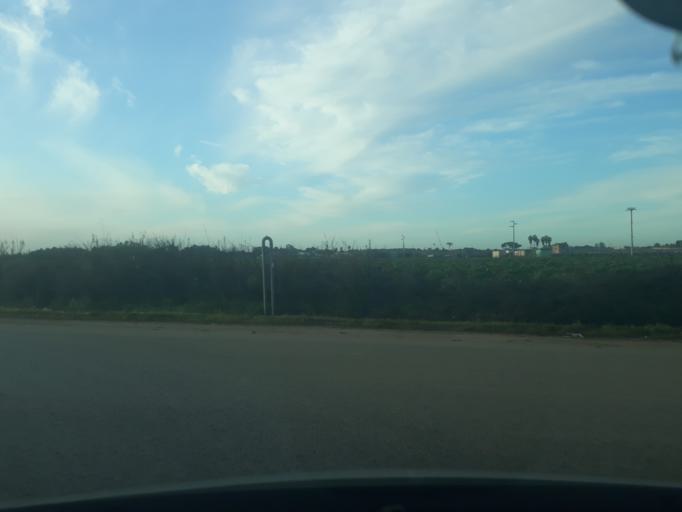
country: IT
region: Apulia
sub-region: Provincia di Brindisi
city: Brindisi
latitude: 40.6561
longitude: 17.8957
